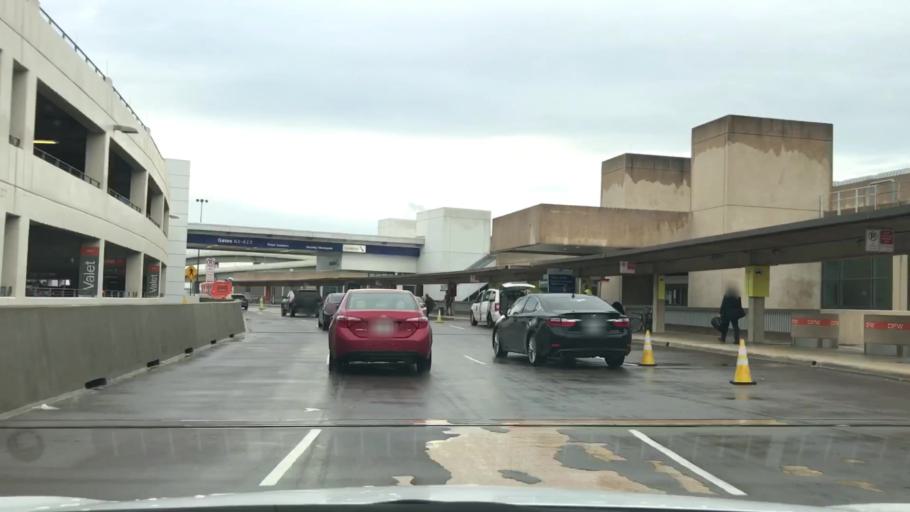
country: US
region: Texas
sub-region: Tarrant County
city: Grapevine
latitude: 32.9063
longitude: -97.0371
